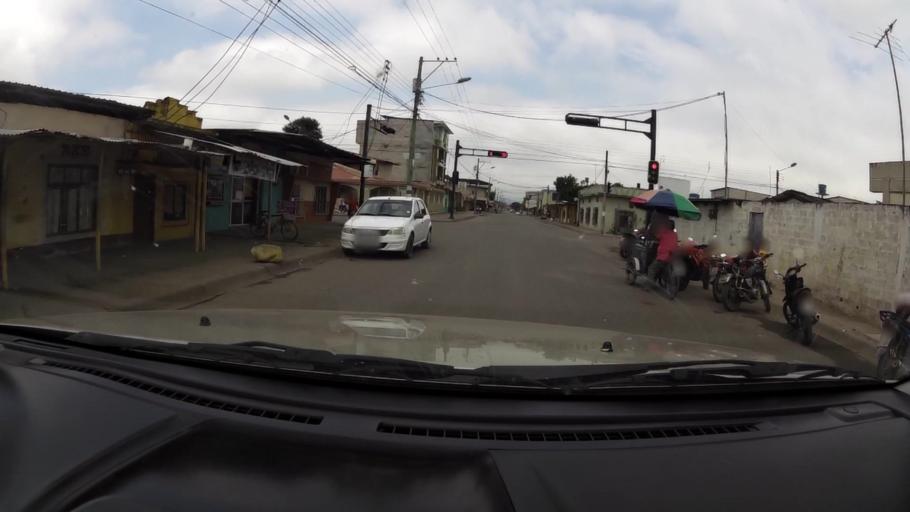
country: EC
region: El Oro
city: Pasaje
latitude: -3.2425
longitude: -79.8297
